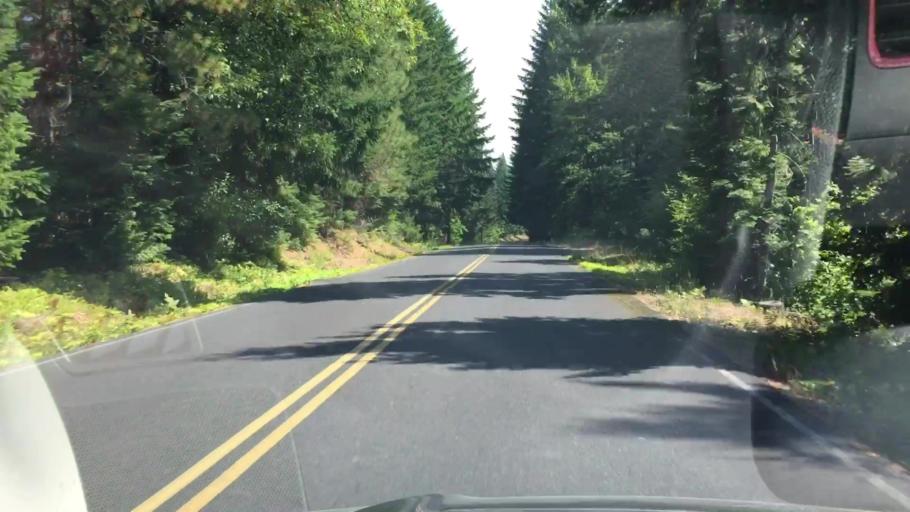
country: US
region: Washington
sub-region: Klickitat County
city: White Salmon
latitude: 46.0430
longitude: -121.5532
